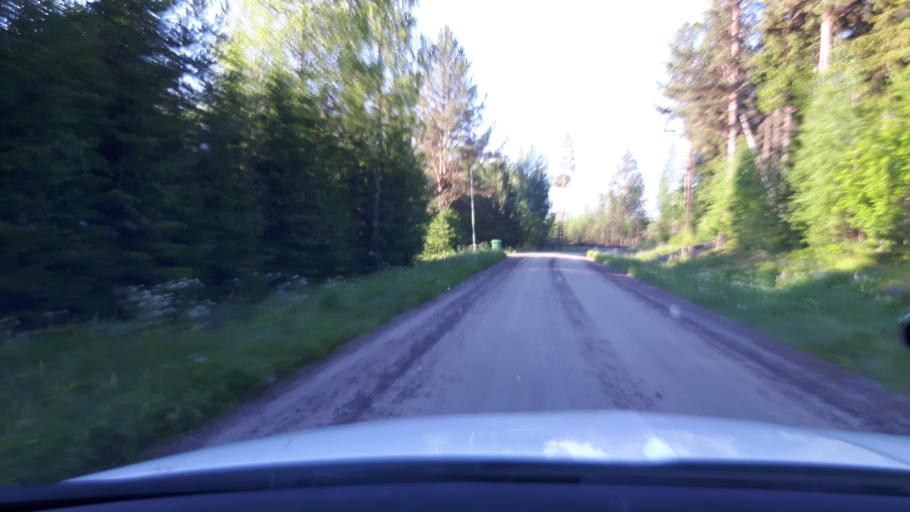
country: SE
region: Vaesternorrland
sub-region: Ange Kommun
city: Ange
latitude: 62.1434
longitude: 15.6615
